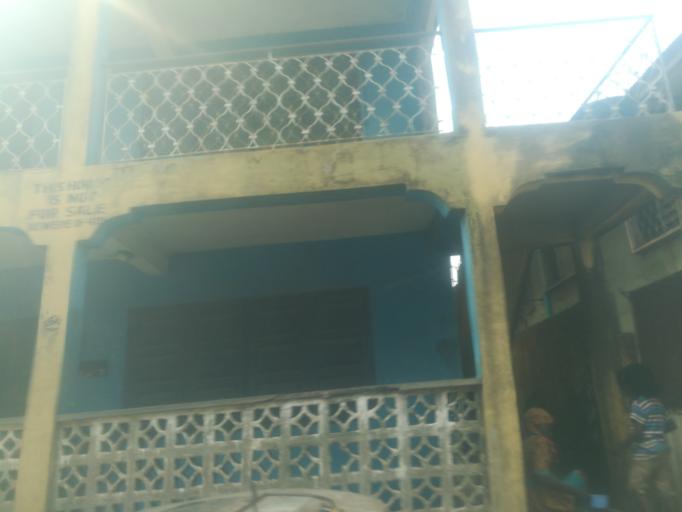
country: NG
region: Oyo
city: Ibadan
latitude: 7.3475
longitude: 3.8769
